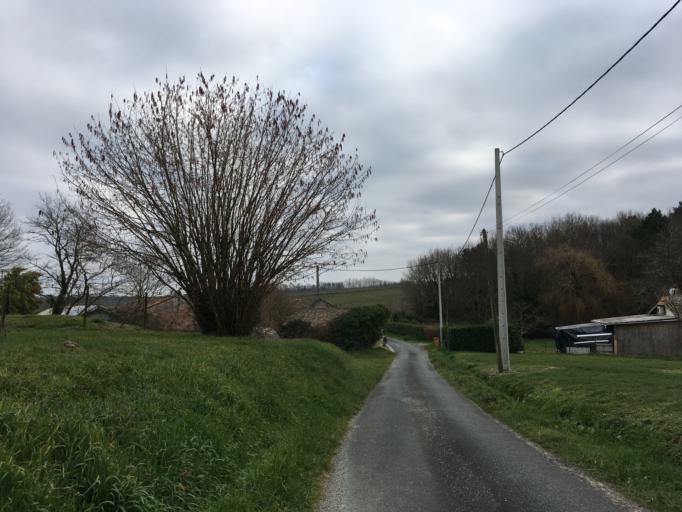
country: FR
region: Aquitaine
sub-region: Departement de la Gironde
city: Saint-Ciers-sur-Gironde
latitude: 45.3126
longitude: -0.5862
